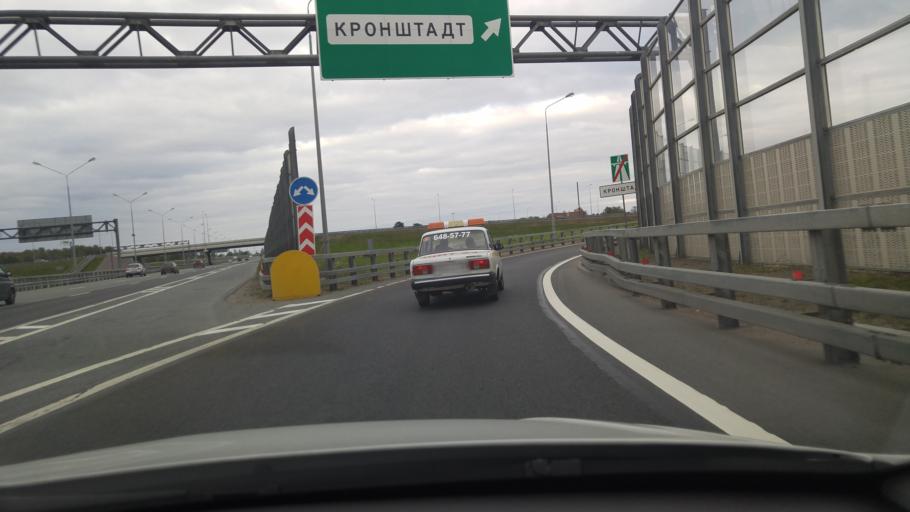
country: RU
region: St.-Petersburg
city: Kronshtadt
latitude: 60.0120
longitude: 29.7171
